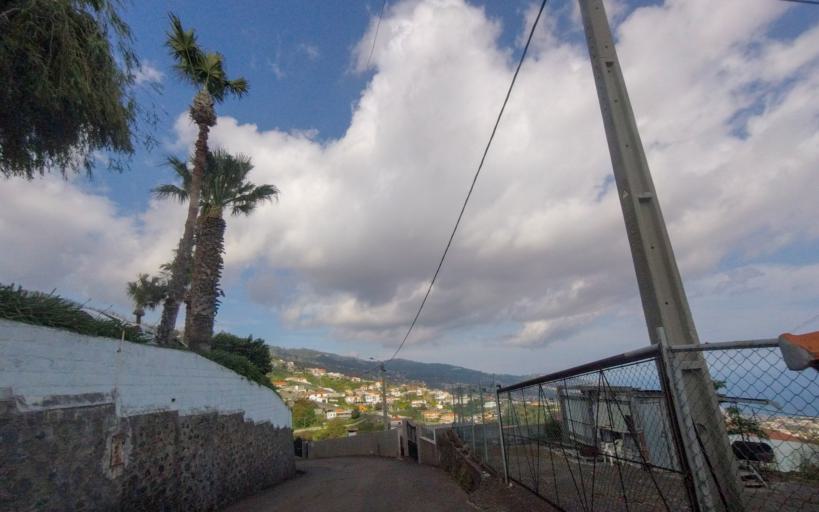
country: PT
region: Madeira
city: Camara de Lobos
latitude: 32.6763
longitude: -16.9465
